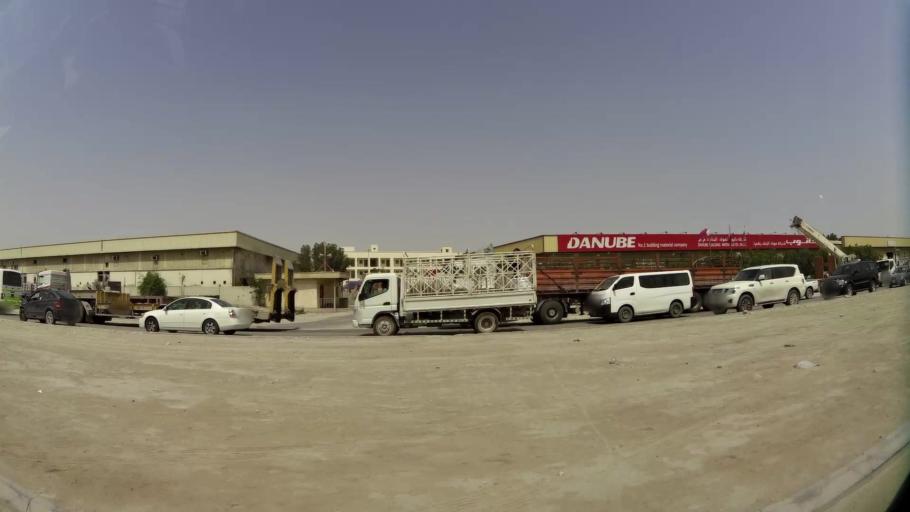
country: QA
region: Baladiyat ar Rayyan
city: Ar Rayyan
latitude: 25.1847
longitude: 51.4321
